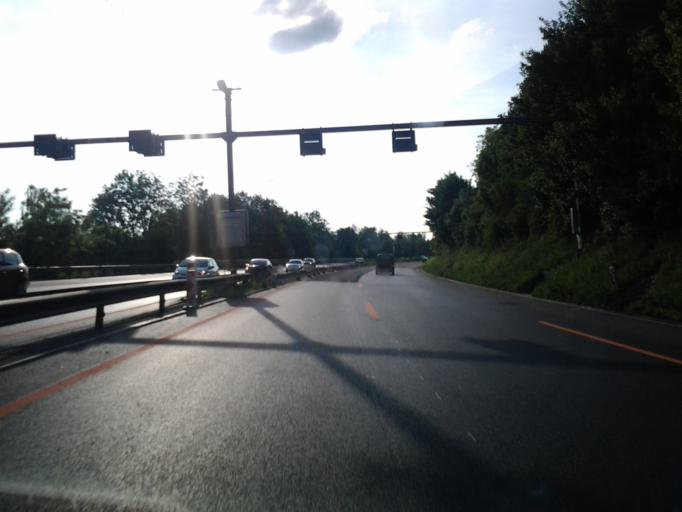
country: CH
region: Lucerne
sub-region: Sursee District
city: Eich
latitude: 47.1531
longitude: 8.1632
